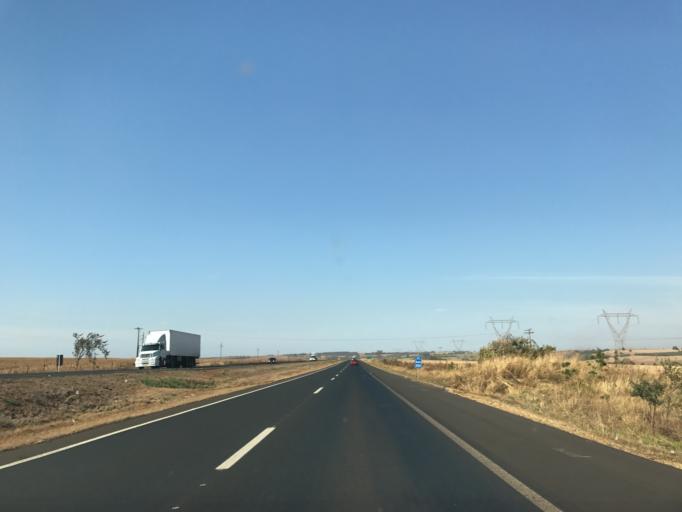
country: BR
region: Goias
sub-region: Goiatuba
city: Goiatuba
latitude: -17.9746
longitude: -49.2555
